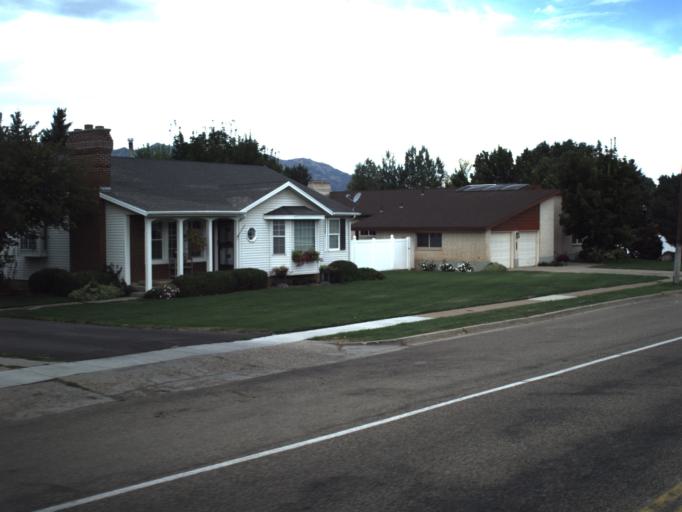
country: US
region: Utah
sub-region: Morgan County
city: Morgan
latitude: 41.0318
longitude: -111.6753
